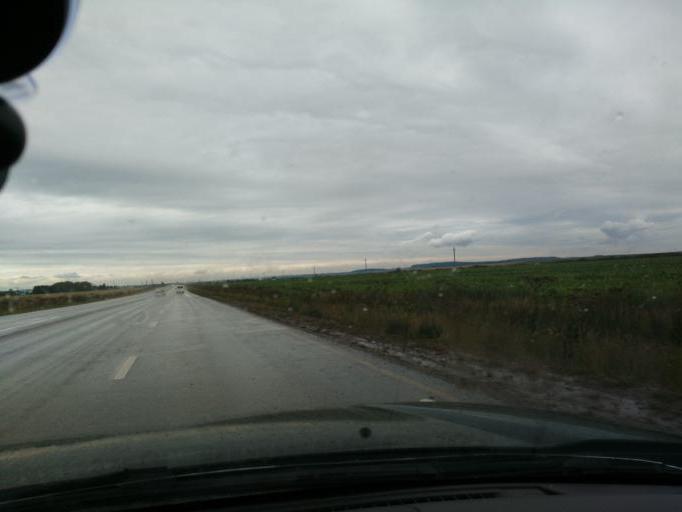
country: RU
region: Perm
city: Kultayevo
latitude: 57.8770
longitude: 55.9068
